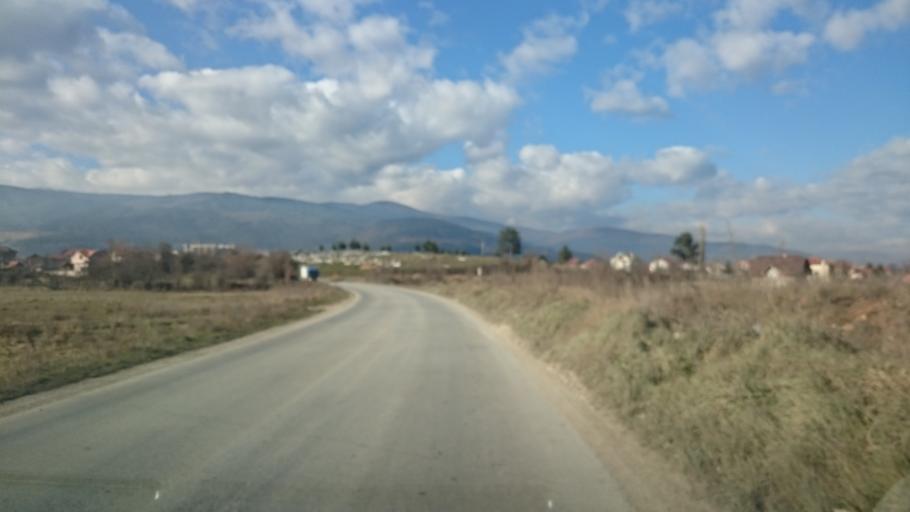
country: MK
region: Kicevo
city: Kicevo
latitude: 41.4986
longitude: 20.9614
